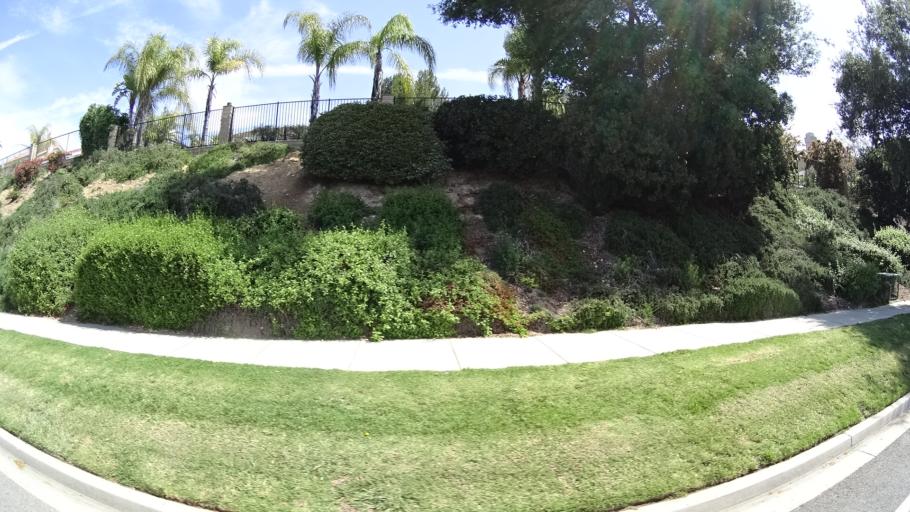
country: US
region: California
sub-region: Ventura County
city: Thousand Oaks
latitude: 34.1967
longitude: -118.8476
